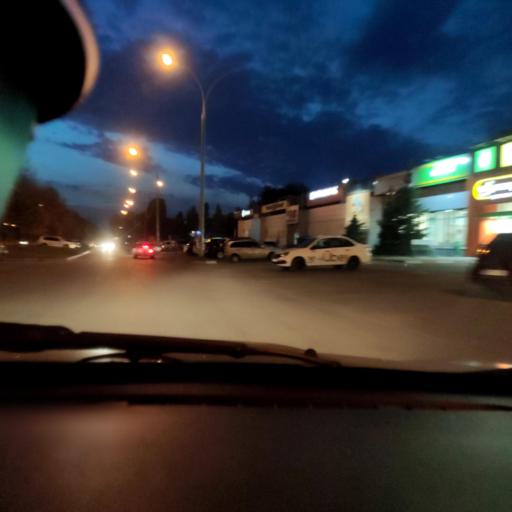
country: RU
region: Samara
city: Tol'yatti
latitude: 53.5179
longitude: 49.3066
